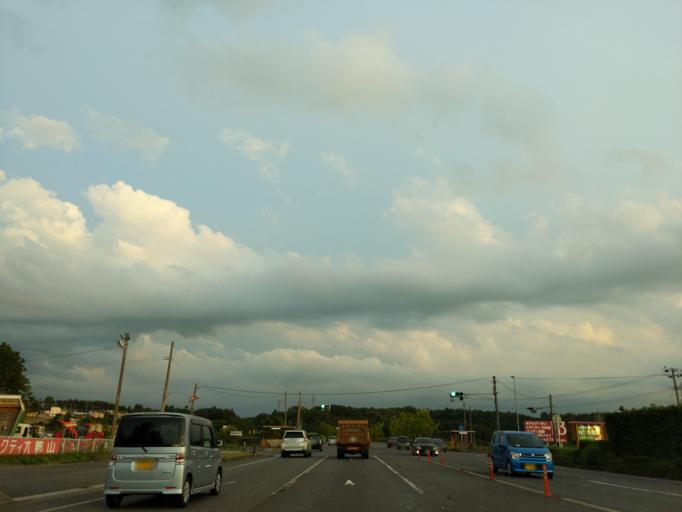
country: JP
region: Fukushima
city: Koriyama
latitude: 37.3646
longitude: 140.3492
